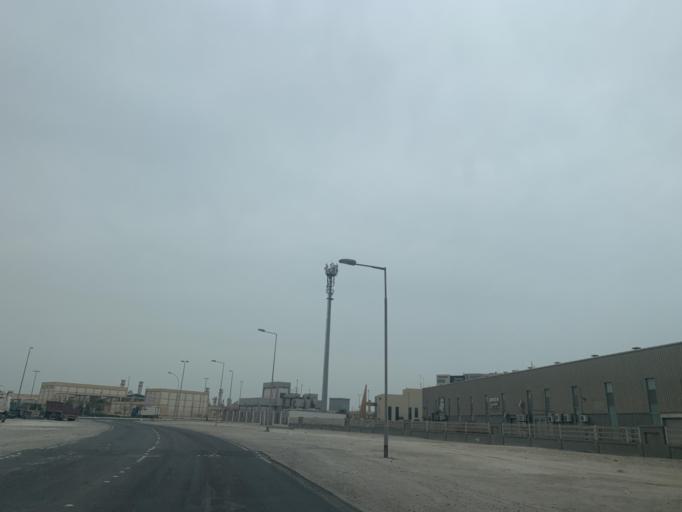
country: BH
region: Muharraq
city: Al Hadd
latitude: 26.2115
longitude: 50.6689
